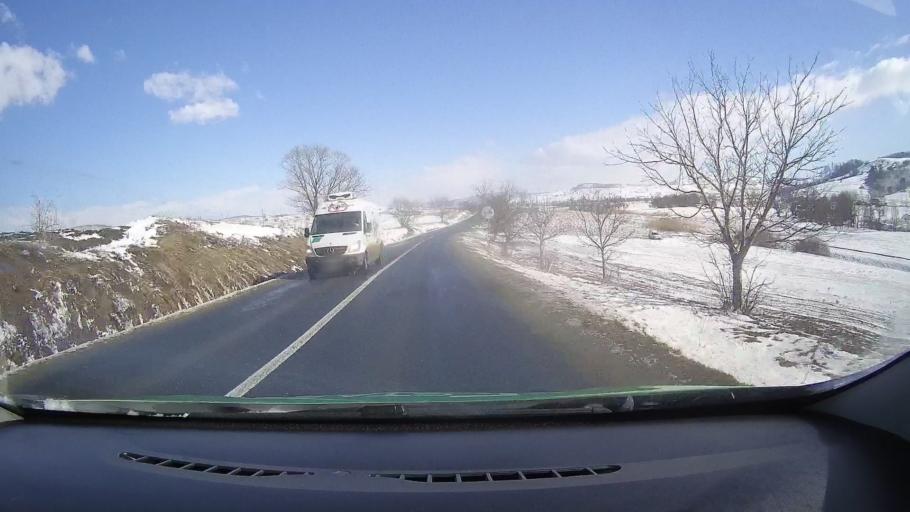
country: RO
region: Sibiu
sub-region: Comuna Rosia
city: Rosia
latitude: 45.7912
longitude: 24.3179
